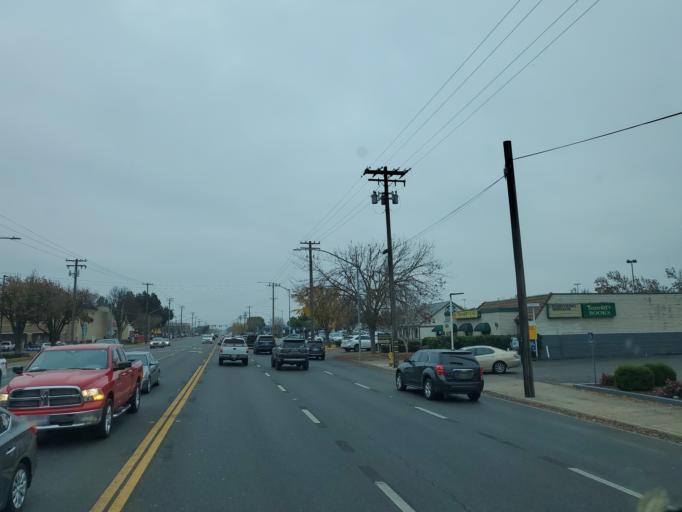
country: US
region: California
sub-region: Stanislaus County
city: Modesto
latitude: 37.6888
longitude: -120.9944
